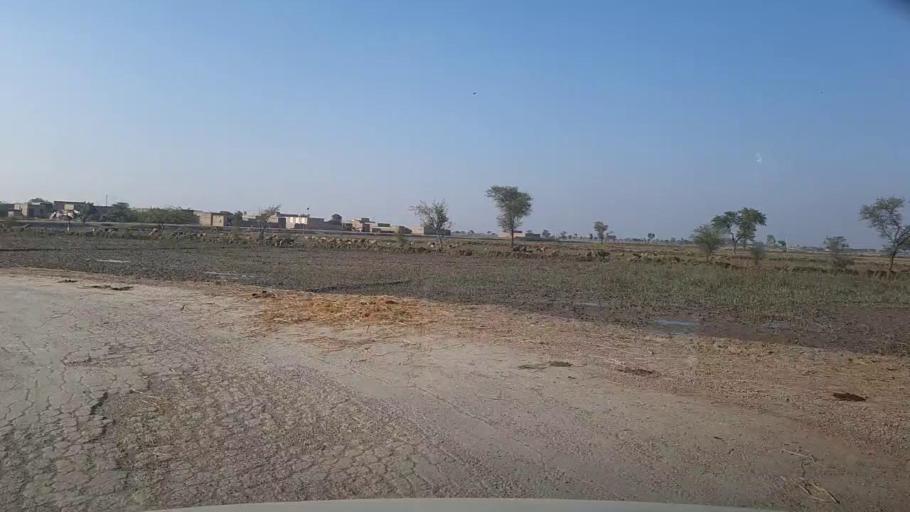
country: PK
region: Sindh
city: Phulji
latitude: 26.8662
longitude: 67.7946
